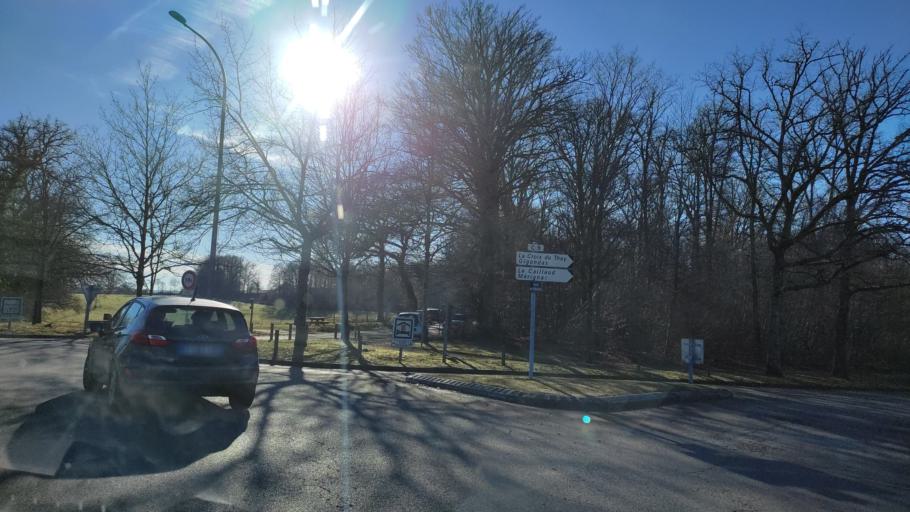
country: FR
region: Limousin
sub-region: Departement de la Haute-Vienne
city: Isle
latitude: 45.7982
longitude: 1.1994
